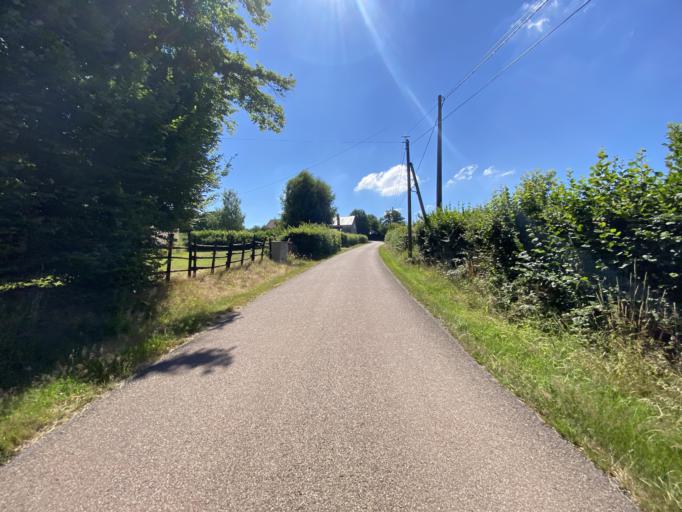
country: FR
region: Bourgogne
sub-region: Departement de la Cote-d'Or
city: Saulieu
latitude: 47.3239
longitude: 4.1519
